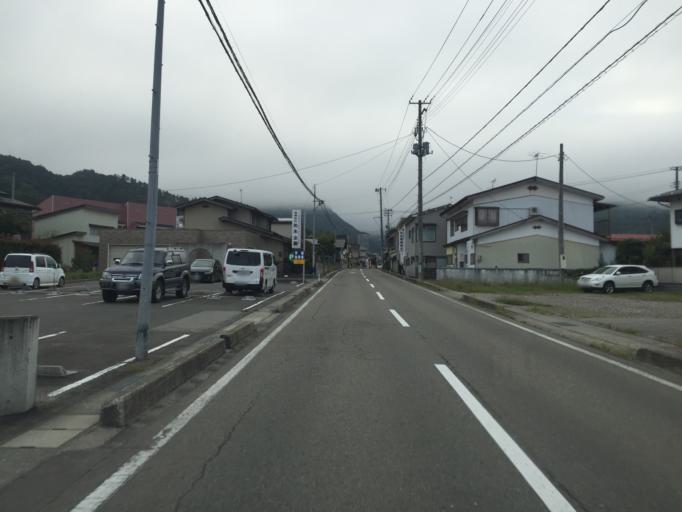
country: JP
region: Fukushima
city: Kitakata
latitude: 37.4916
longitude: 139.9462
